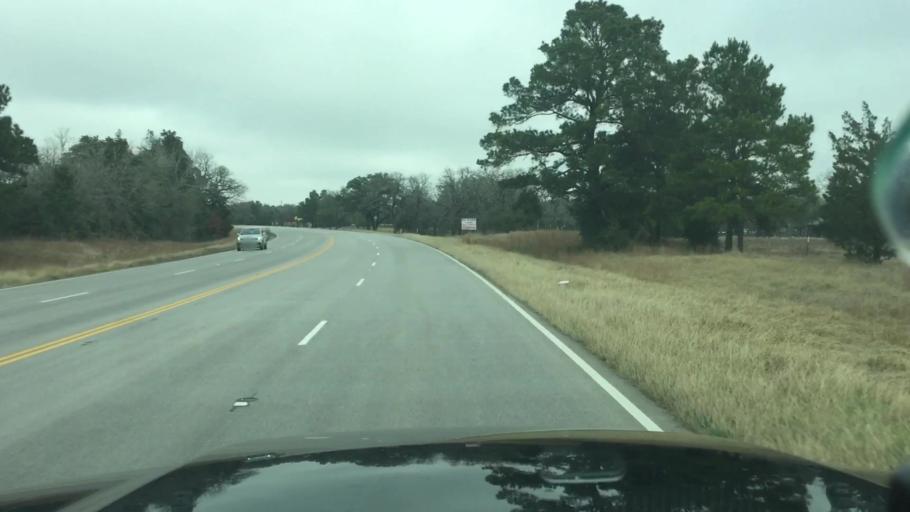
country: US
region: Texas
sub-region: Lee County
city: Giddings
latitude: 30.0922
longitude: -96.9132
